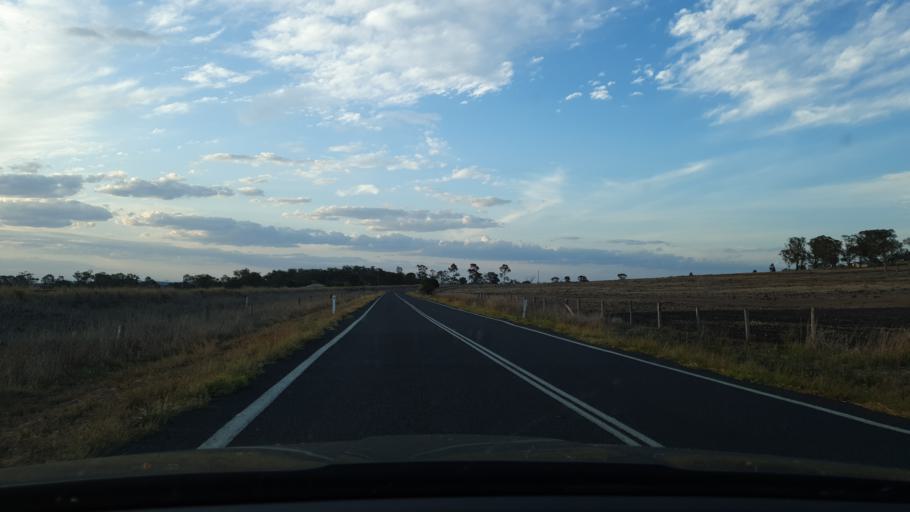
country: AU
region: Queensland
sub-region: Southern Downs
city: Warwick
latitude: -28.1808
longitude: 151.9774
